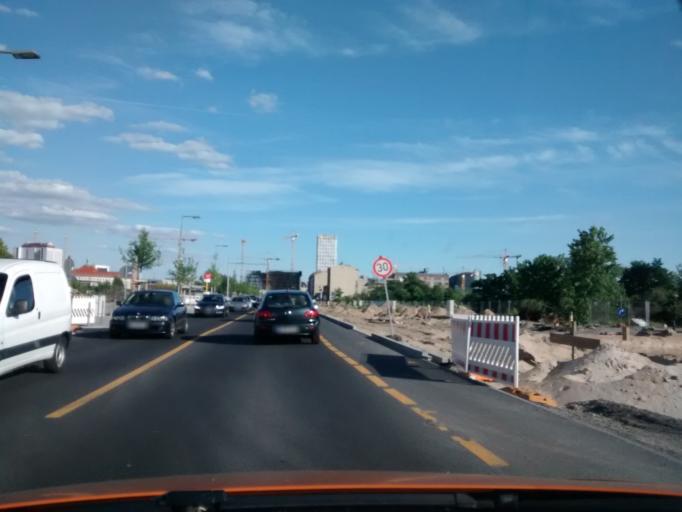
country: DE
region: Berlin
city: Wedding Bezirk
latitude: 52.5339
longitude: 13.3650
